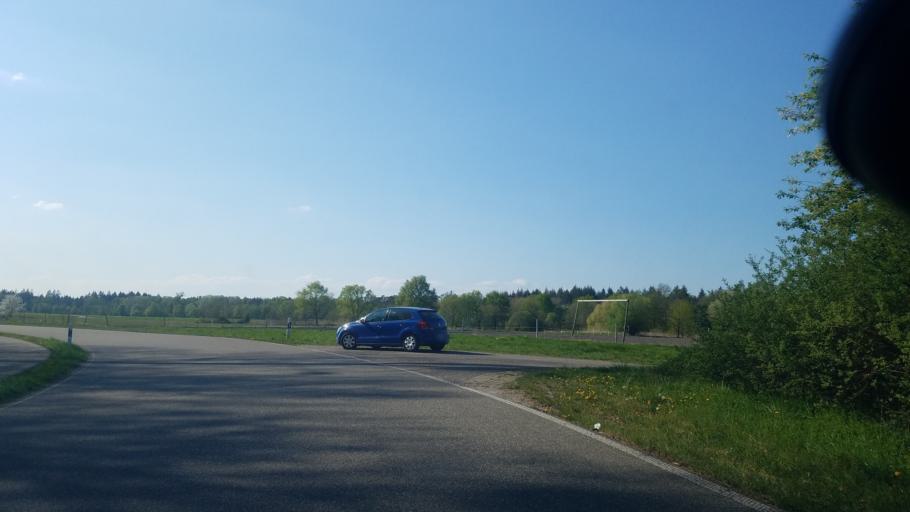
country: DE
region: Baden-Wuerttemberg
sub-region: Karlsruhe Region
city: Hugelsheim
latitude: 48.7696
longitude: 8.1107
